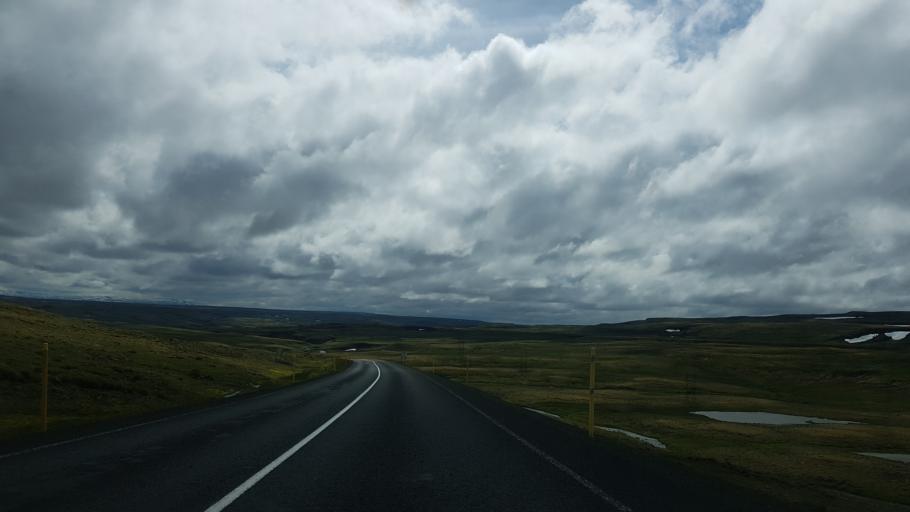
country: IS
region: West
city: Borgarnes
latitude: 64.9739
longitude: -21.0671
